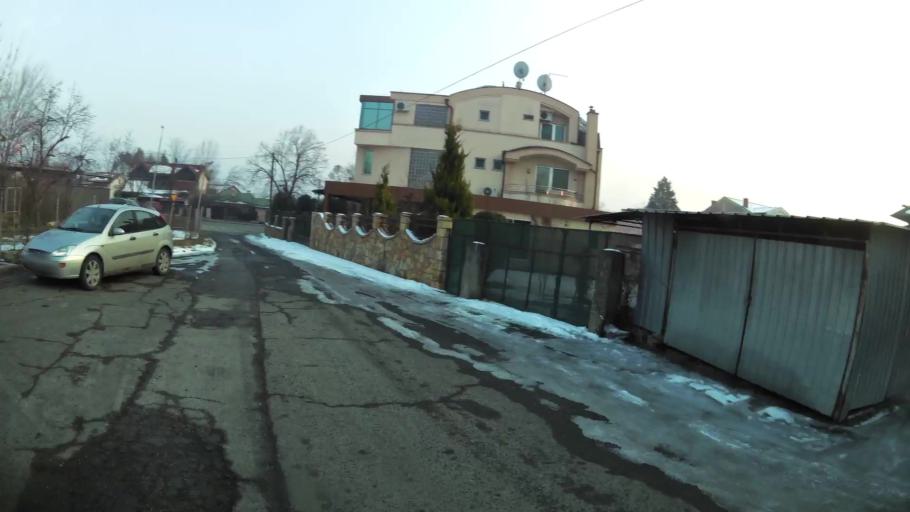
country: MK
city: Creshevo
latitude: 42.0092
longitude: 21.5076
